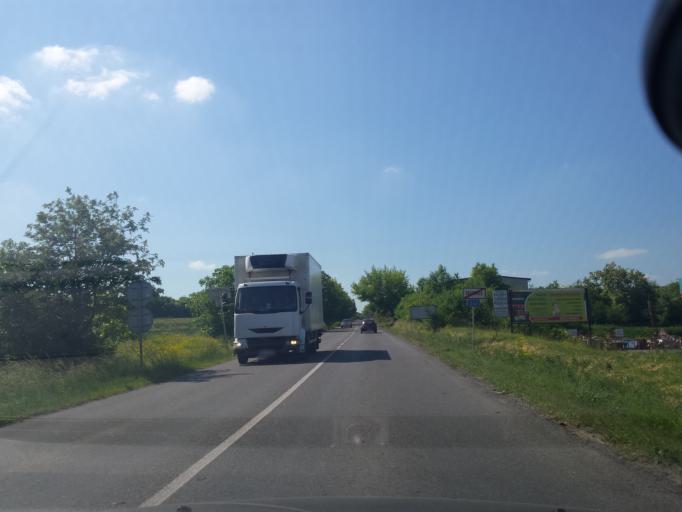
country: CZ
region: Central Bohemia
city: Velke Prilepy
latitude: 50.1491
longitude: 14.3273
